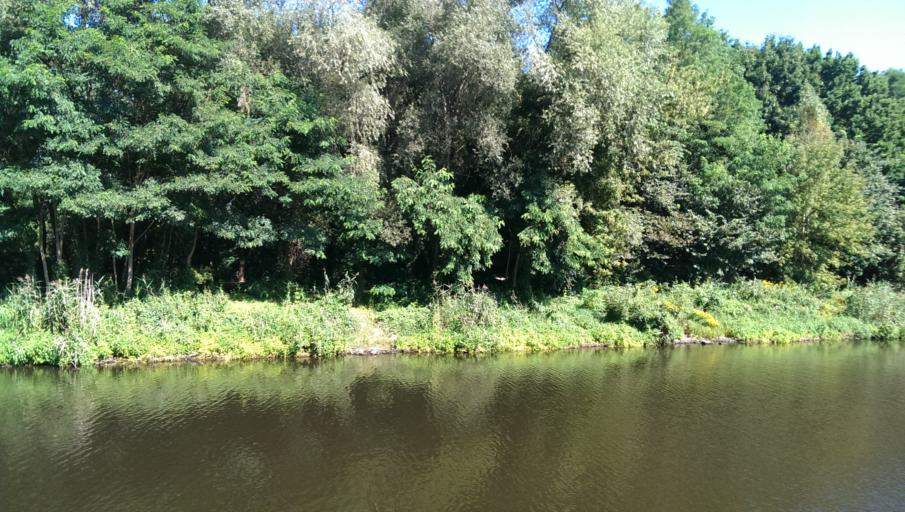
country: DE
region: Brandenburg
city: Stahnsdorf
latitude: 52.3954
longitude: 13.2044
